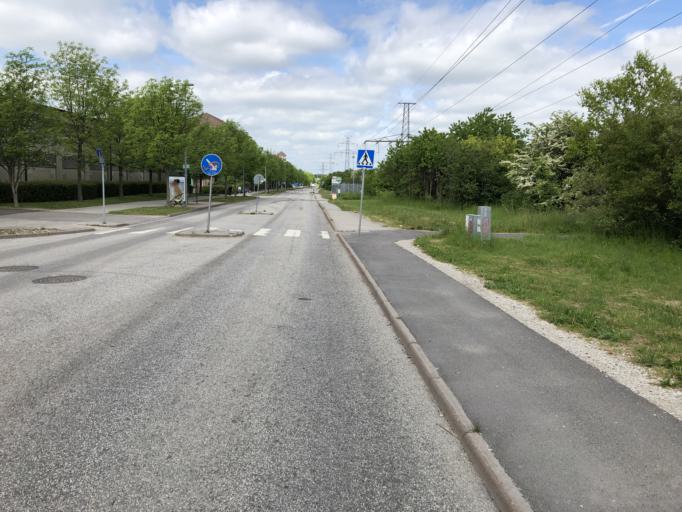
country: SE
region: Skane
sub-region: Lunds Kommun
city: Lund
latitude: 55.7046
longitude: 13.1611
